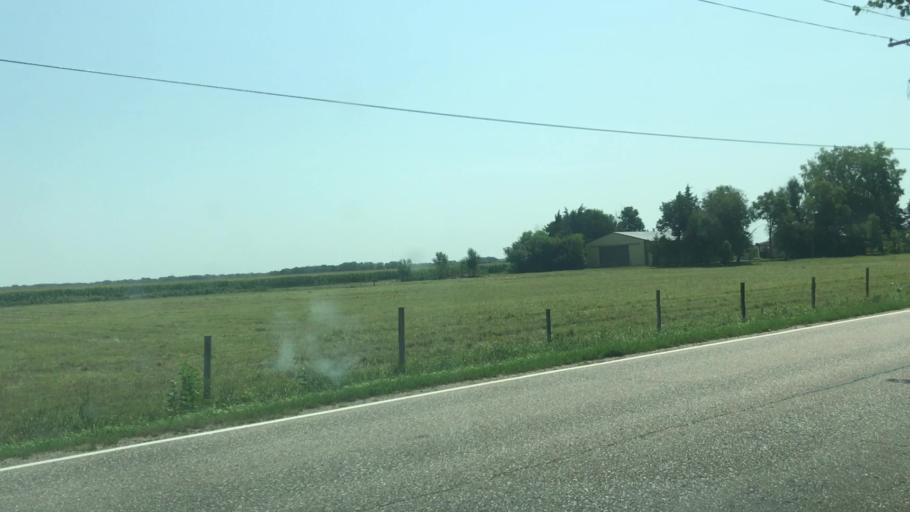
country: US
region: Nebraska
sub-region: Hall County
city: Grand Island
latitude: 40.8935
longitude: -98.3017
